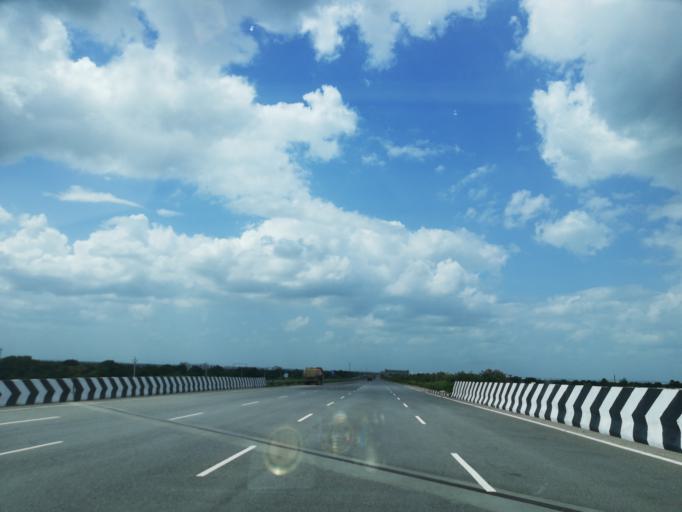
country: IN
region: Telangana
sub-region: Medak
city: Serilingampalle
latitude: 17.4725
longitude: 78.2480
